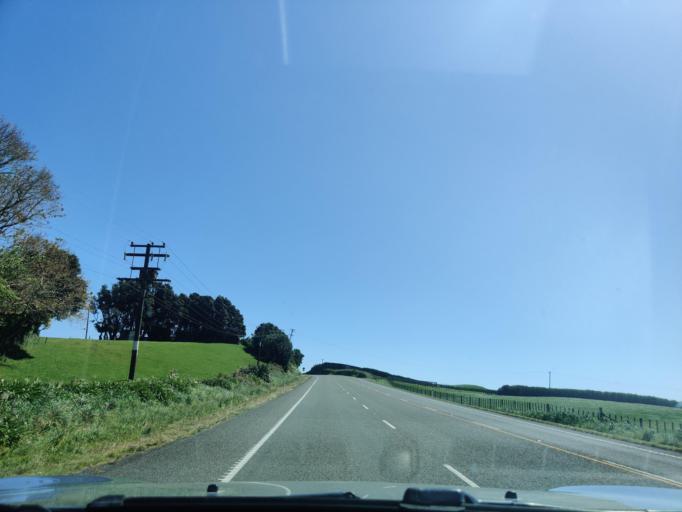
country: NZ
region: Taranaki
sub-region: South Taranaki District
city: Patea
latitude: -39.6813
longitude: 174.4156
